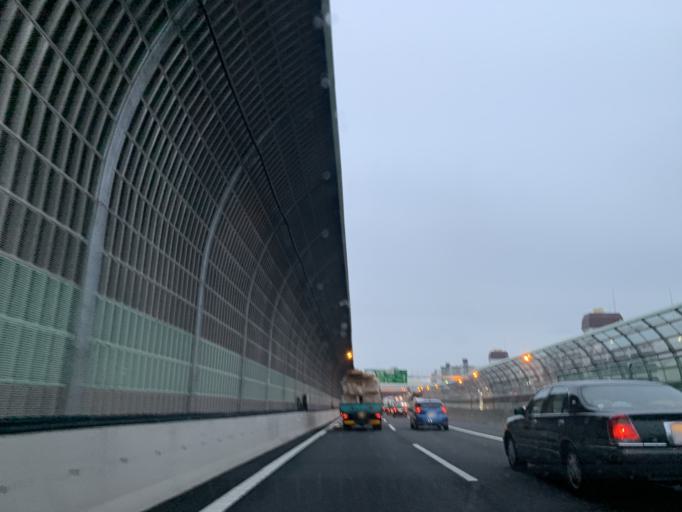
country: JP
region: Chiba
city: Funabashi
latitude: 35.6841
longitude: 140.0053
